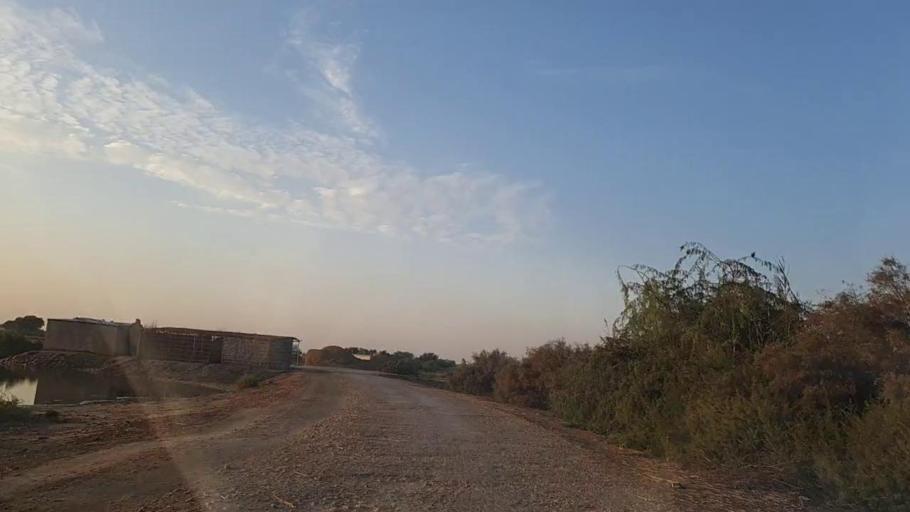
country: PK
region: Sindh
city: Chuhar Jamali
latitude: 24.4556
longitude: 68.1168
